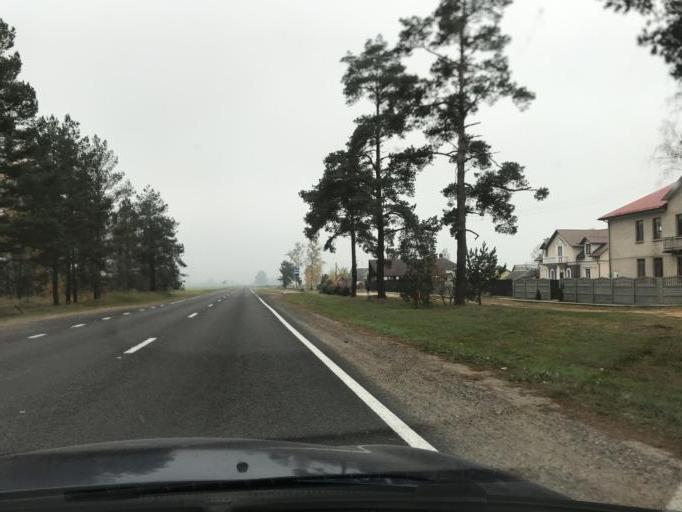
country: BY
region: Grodnenskaya
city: Hrodna
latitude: 53.8309
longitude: 23.8843
